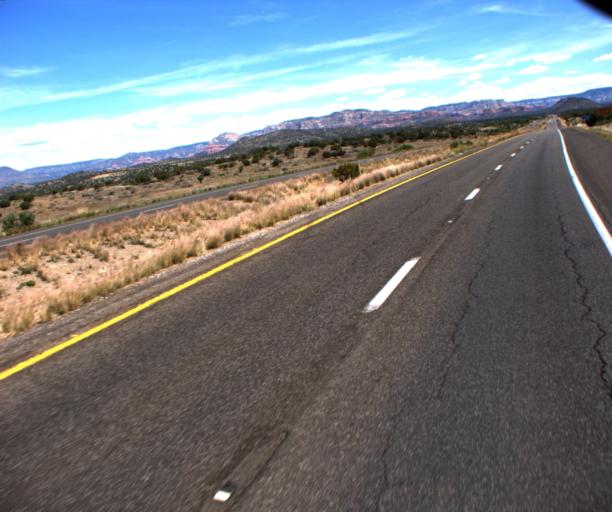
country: US
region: Arizona
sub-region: Yavapai County
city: Cornville
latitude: 34.8053
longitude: -111.9105
